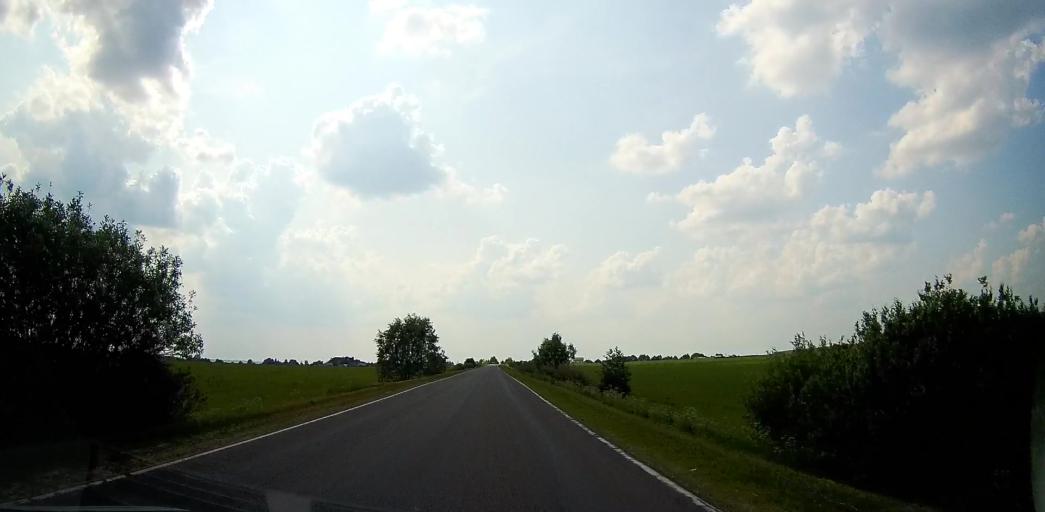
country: RU
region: Moskovskaya
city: Malino
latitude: 55.0644
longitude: 38.1175
